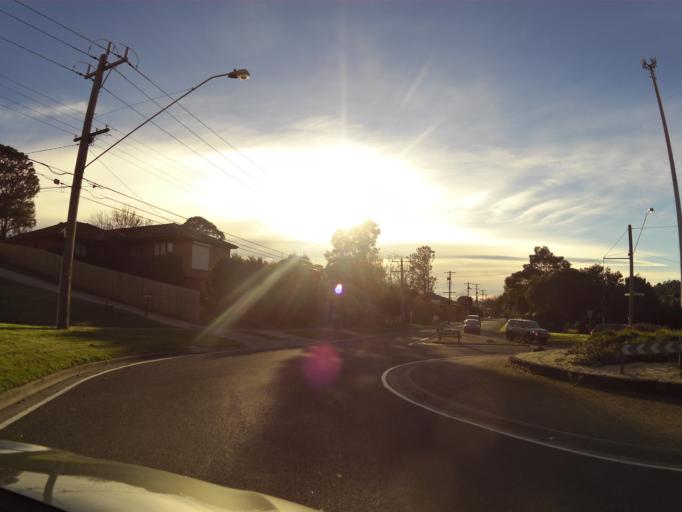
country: AU
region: Victoria
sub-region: Knox
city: Ferntree Gully
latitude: -37.8945
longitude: 145.2926
